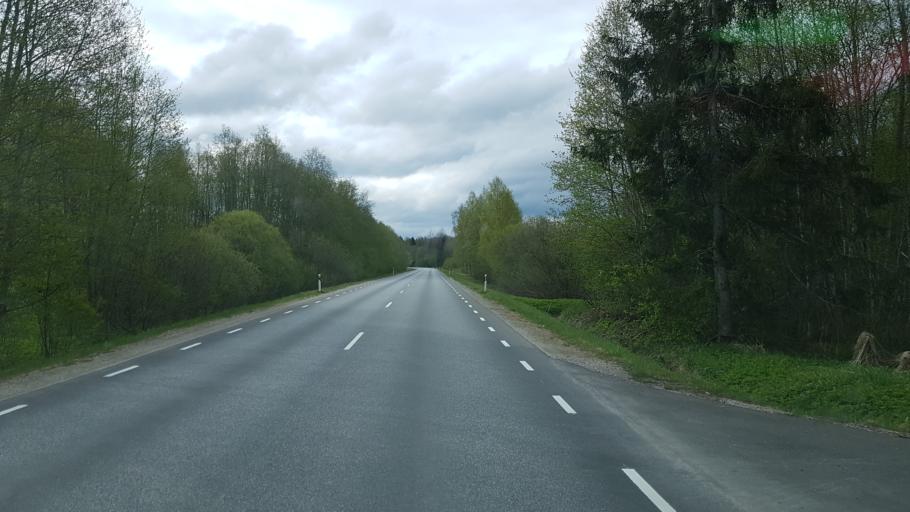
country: EE
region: Harju
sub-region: Anija vald
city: Kehra
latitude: 59.3036
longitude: 25.3580
